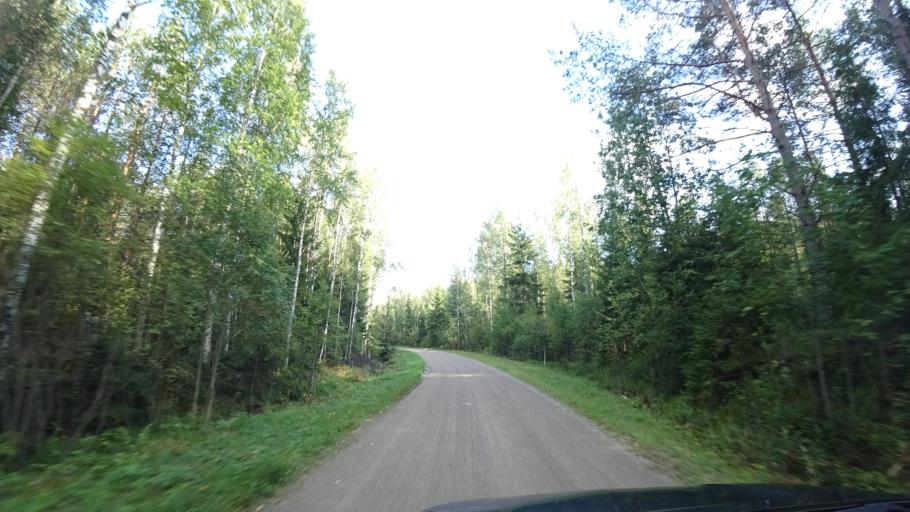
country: FI
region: Paijanne Tavastia
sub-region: Lahti
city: Auttoinen
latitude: 61.2131
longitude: 25.1609
